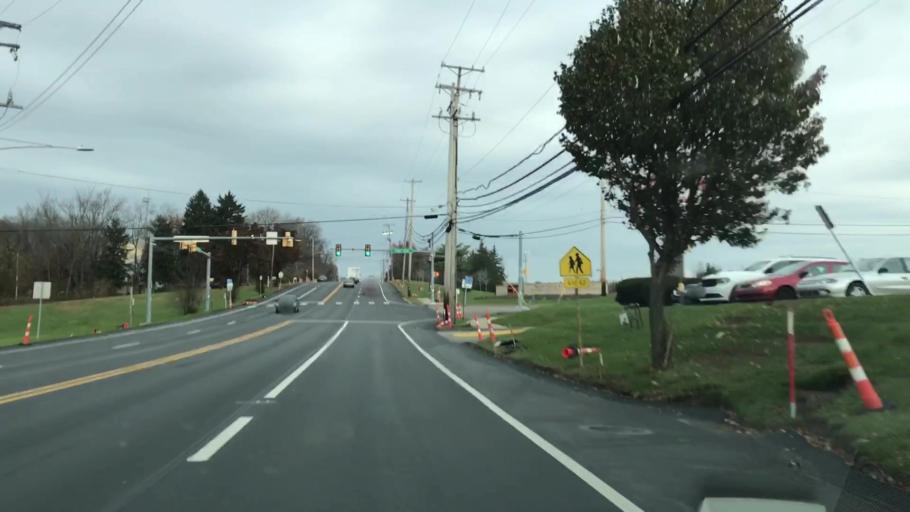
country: US
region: Pennsylvania
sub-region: Allegheny County
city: Carnot-Moon
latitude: 40.5085
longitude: -80.2231
